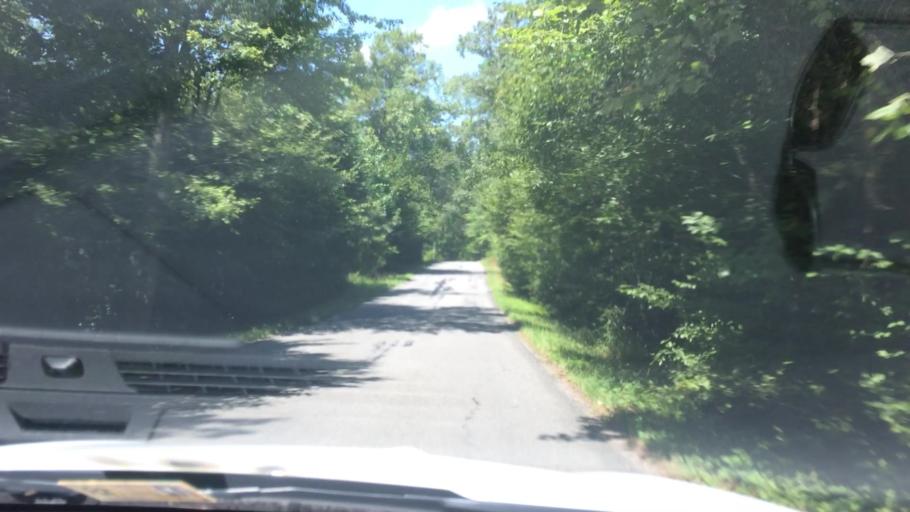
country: US
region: Virginia
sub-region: Charles City County
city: Charles City
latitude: 37.2789
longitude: -76.9290
